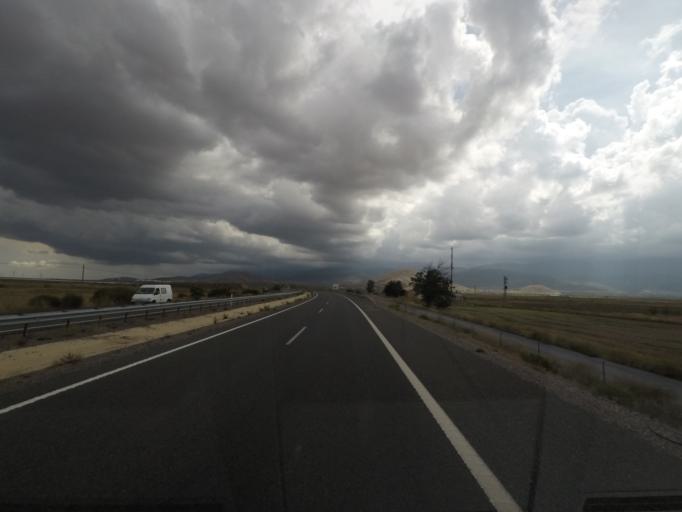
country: ES
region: Andalusia
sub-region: Provincia de Granada
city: Aldeire
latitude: 37.2139
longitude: -3.0713
